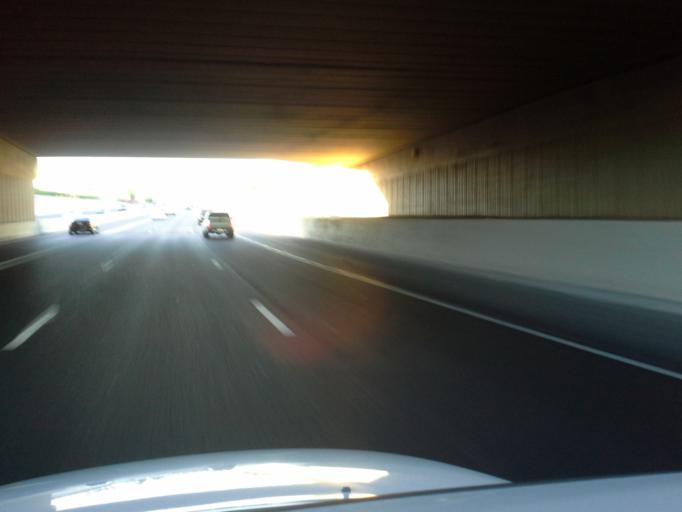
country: US
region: Arizona
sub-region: Maricopa County
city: Glendale
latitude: 33.5674
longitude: -112.1172
